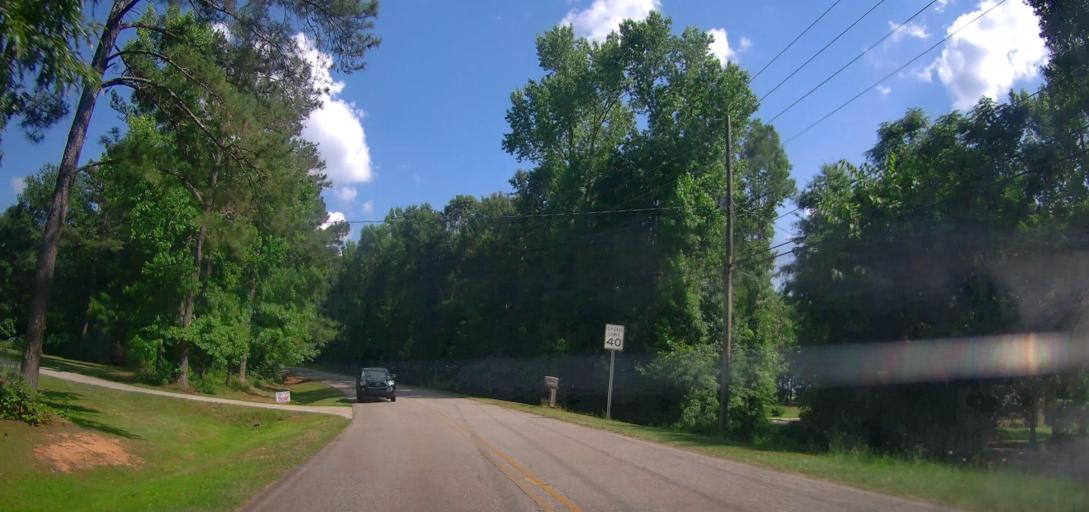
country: US
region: Georgia
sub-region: Spalding County
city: East Griffin
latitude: 33.2293
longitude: -84.1282
